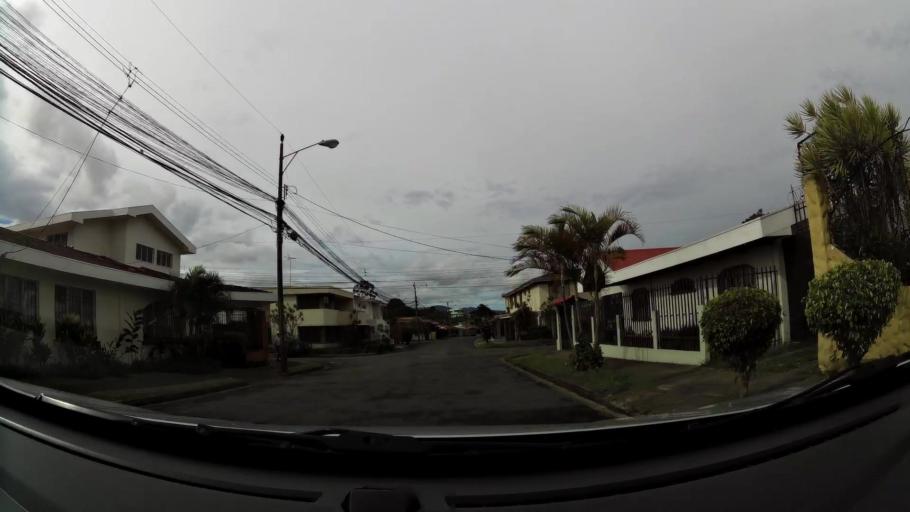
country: CR
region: San Jose
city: San Vicente de Moravia
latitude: 9.9601
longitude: -84.0576
